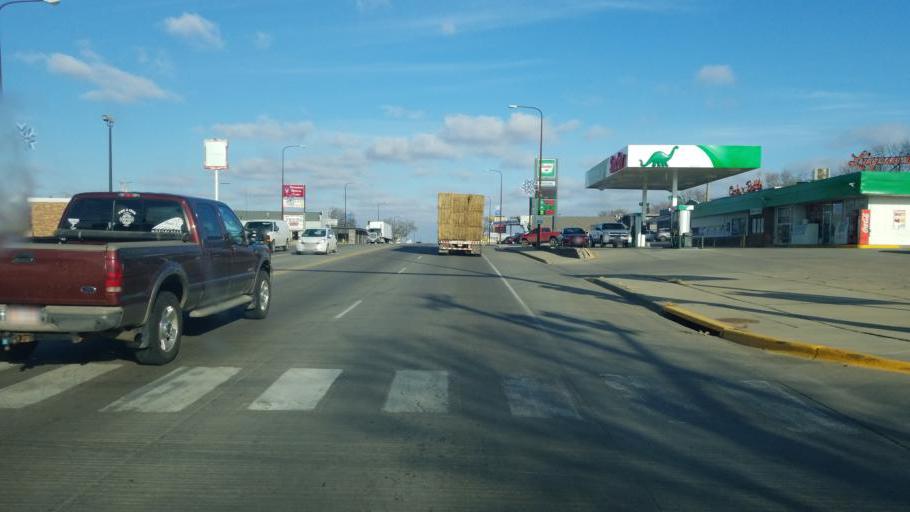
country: US
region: South Dakota
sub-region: Yankton County
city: Yankton
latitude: 42.8835
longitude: -97.3966
